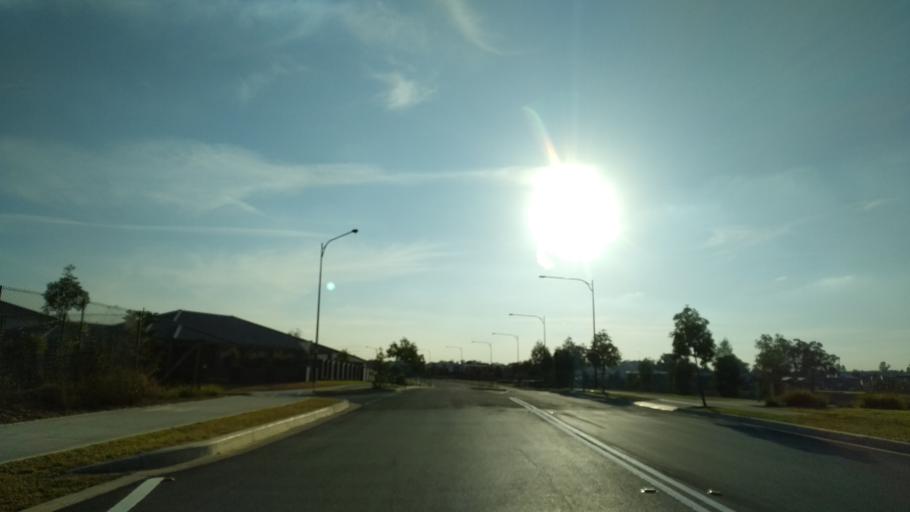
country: AU
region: New South Wales
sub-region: Penrith Municipality
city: Werrington Downs
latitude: -33.7294
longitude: 150.7386
